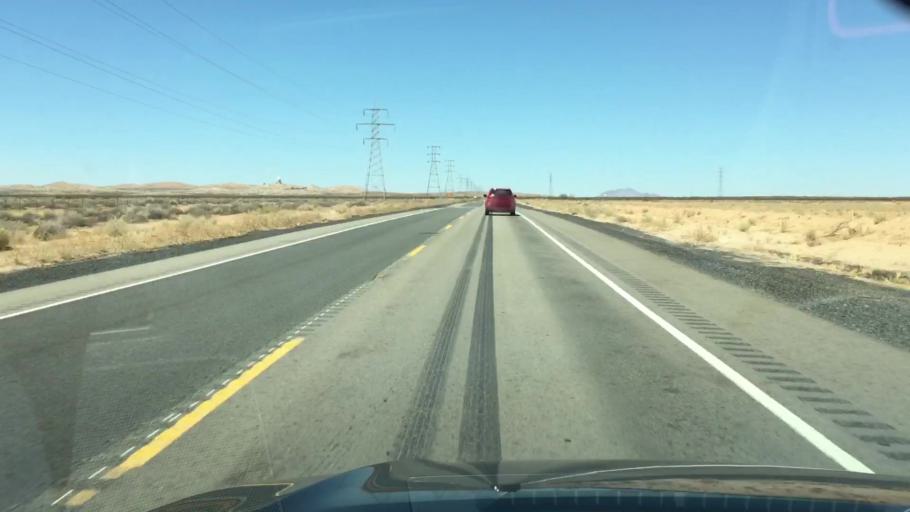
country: US
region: California
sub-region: Kern County
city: Boron
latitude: 35.0311
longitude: -117.5524
